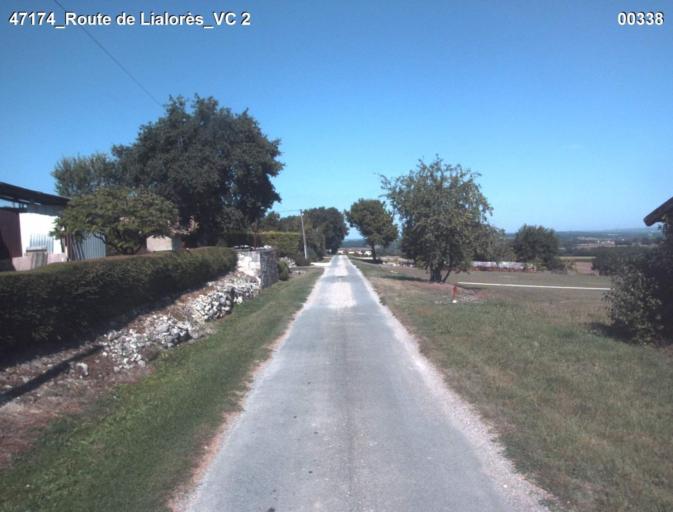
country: FR
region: Midi-Pyrenees
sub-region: Departement du Gers
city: Condom
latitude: 44.0103
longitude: 0.3809
